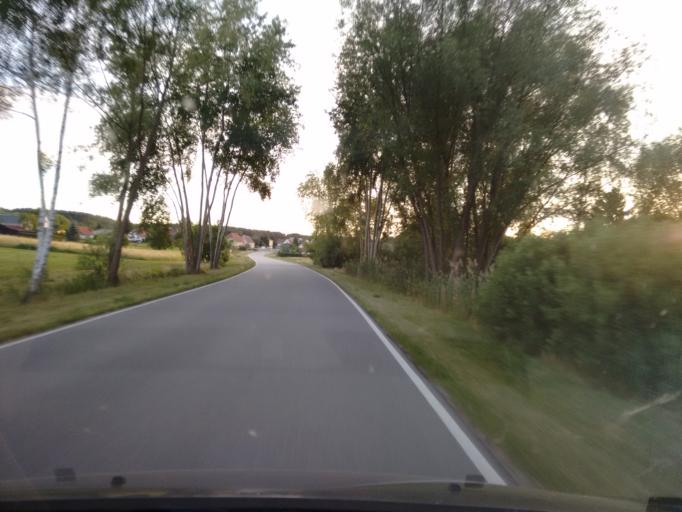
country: DE
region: Brandenburg
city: Gross Lindow
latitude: 52.1392
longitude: 14.4914
